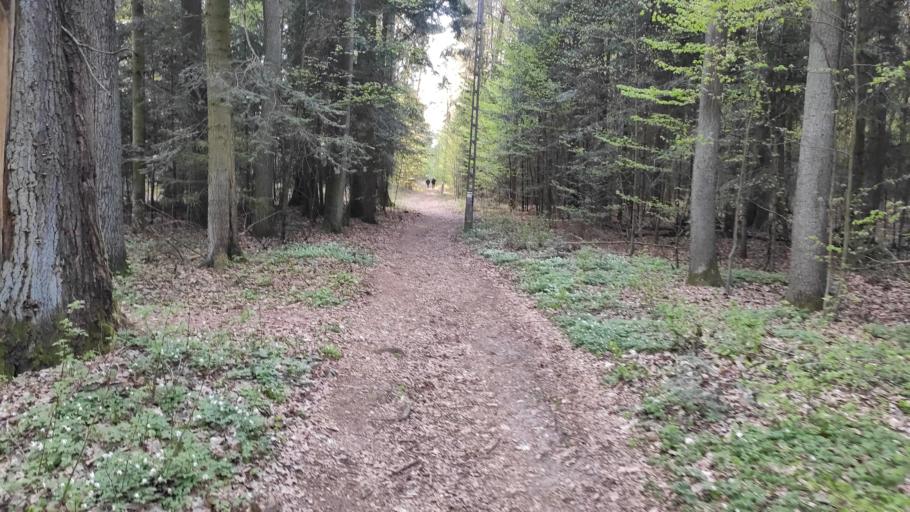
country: PL
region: Masovian Voivodeship
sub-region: Powiat radomski
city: Pionki
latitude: 51.4757
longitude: 21.4352
